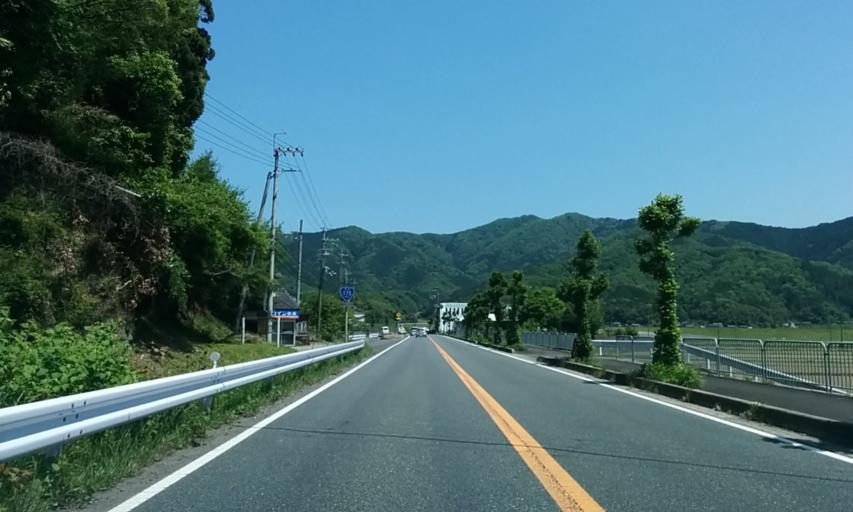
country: JP
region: Kyoto
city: Fukuchiyama
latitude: 35.3394
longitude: 135.1036
